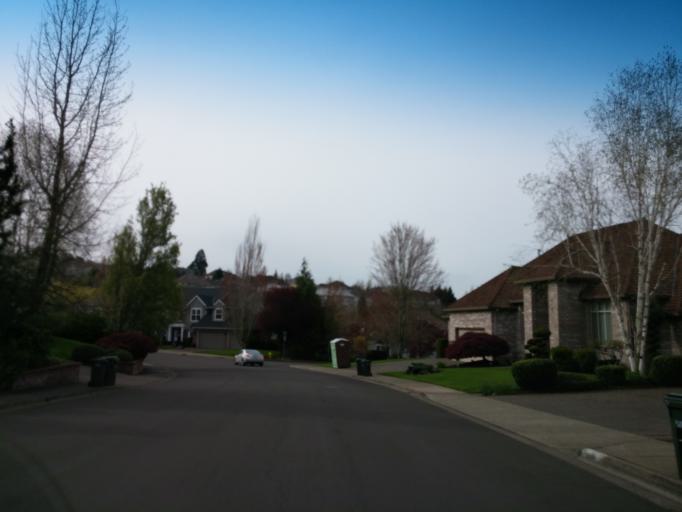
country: US
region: Oregon
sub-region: Washington County
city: Cedar Mill
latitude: 45.5395
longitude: -122.8084
